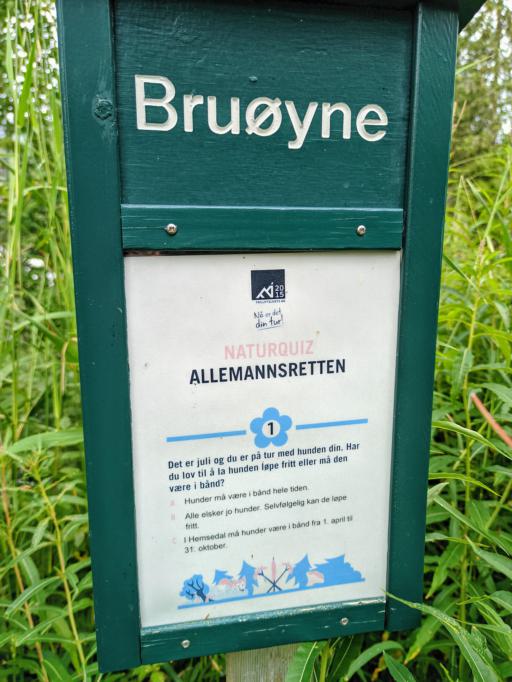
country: NO
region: Buskerud
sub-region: Hemsedal
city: Hemsedal
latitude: 60.8613
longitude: 8.5536
